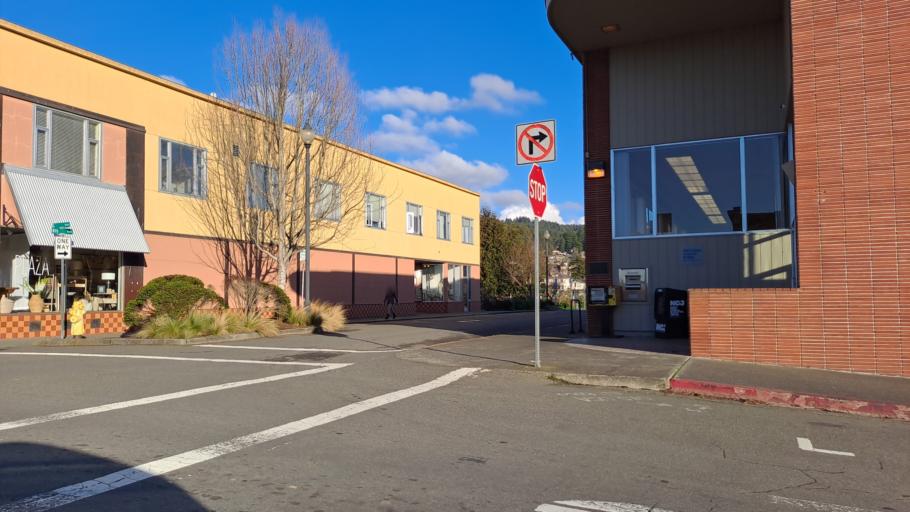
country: US
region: California
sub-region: Humboldt County
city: Arcata
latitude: 40.8679
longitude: -124.0861
